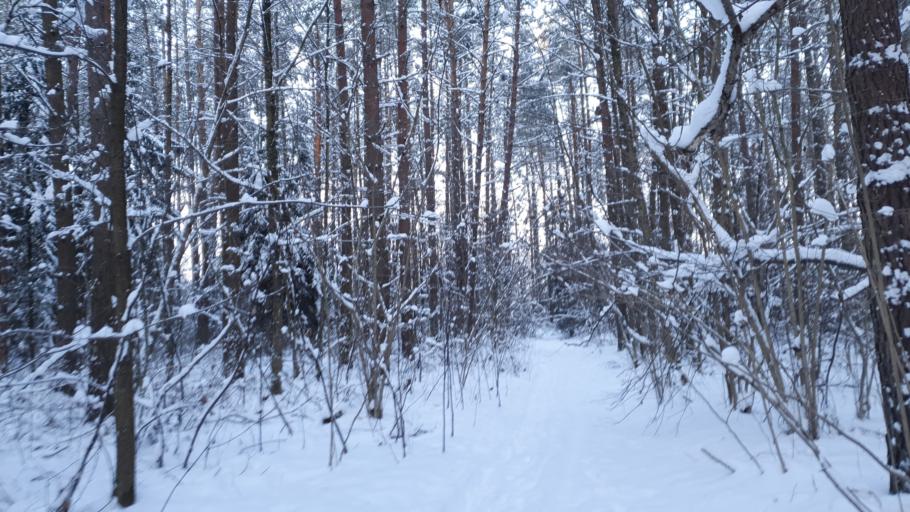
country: LT
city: Skaidiskes
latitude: 54.6454
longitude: 25.4214
